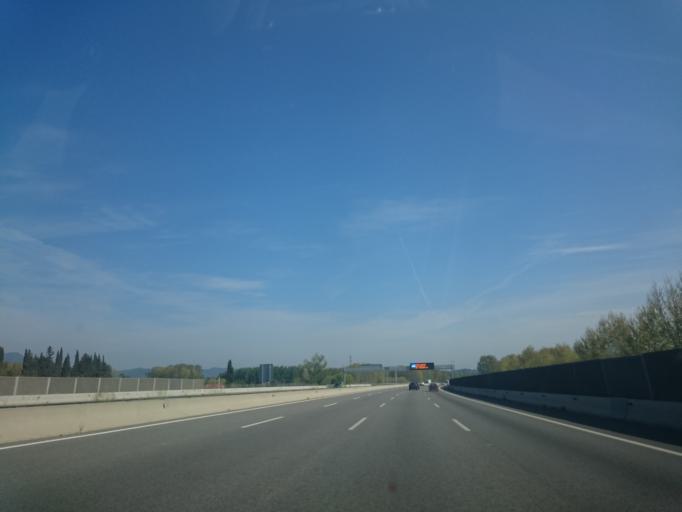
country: ES
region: Catalonia
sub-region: Provincia de Girona
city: Salt
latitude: 41.9741
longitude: 2.7785
